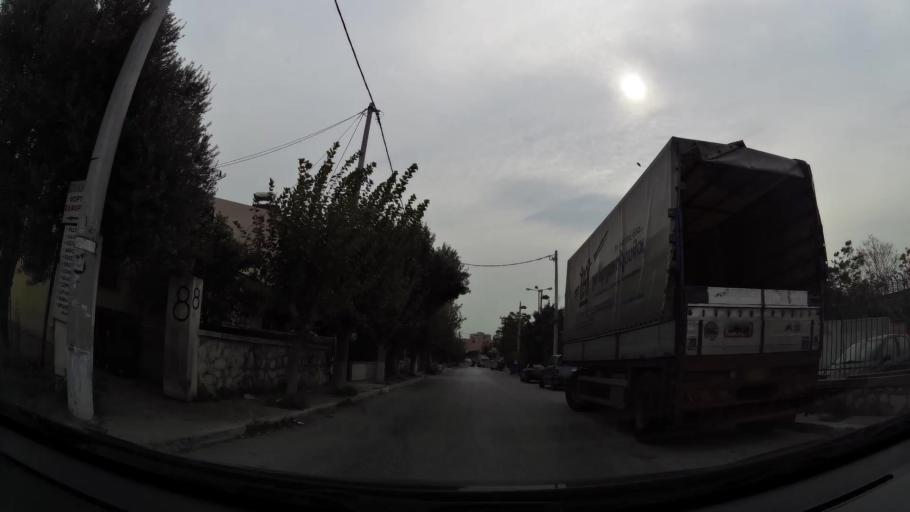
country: GR
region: Attica
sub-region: Nomarchia Athinas
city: Tavros
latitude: 37.9730
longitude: 23.6952
